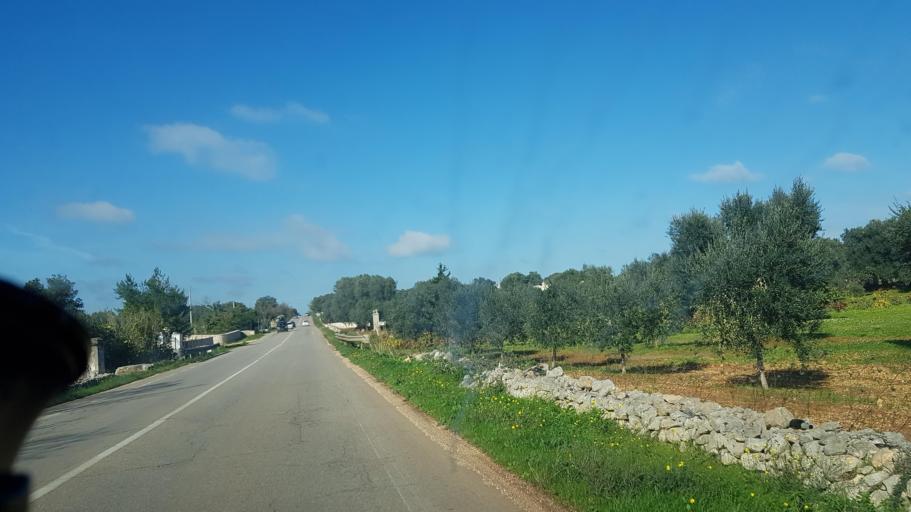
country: IT
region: Apulia
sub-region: Provincia di Brindisi
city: Carovigno
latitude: 40.6840
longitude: 17.6804
